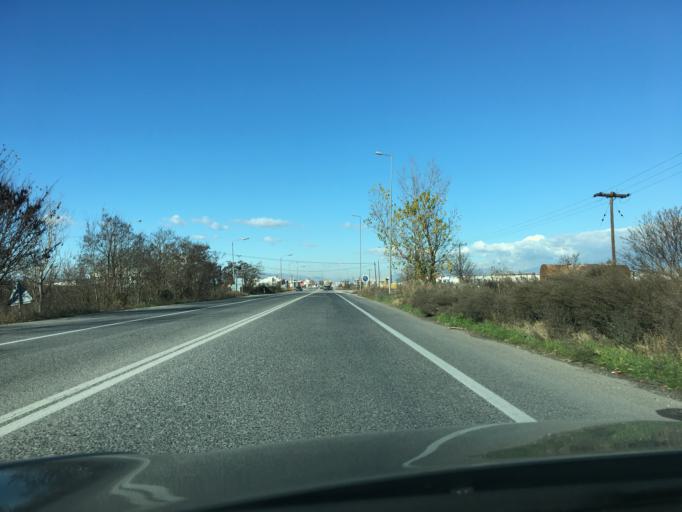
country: GR
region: Thessaly
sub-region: Nomos Larisis
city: Nikaia
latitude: 39.6014
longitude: 22.4445
